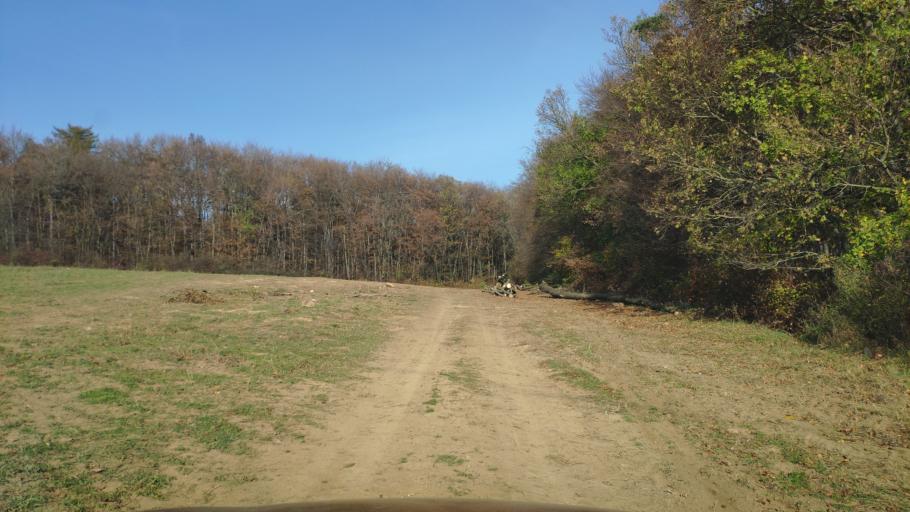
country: SK
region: Presovsky
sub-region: Okres Presov
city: Presov
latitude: 48.8949
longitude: 21.2268
